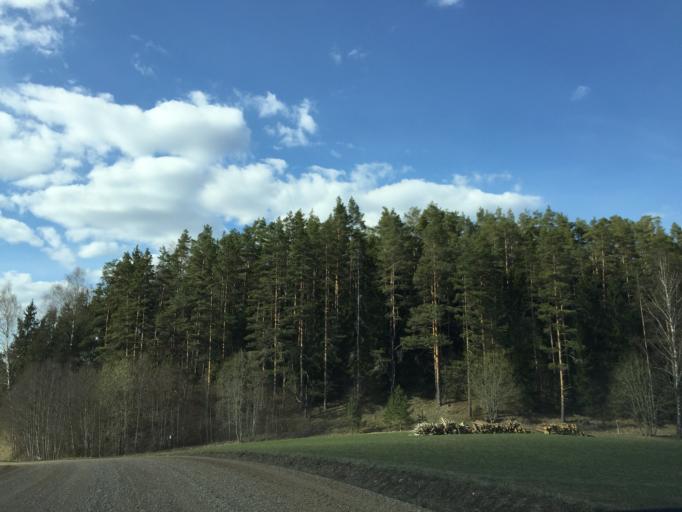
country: EE
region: Tartu
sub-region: Elva linn
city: Elva
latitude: 58.1008
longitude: 26.5071
